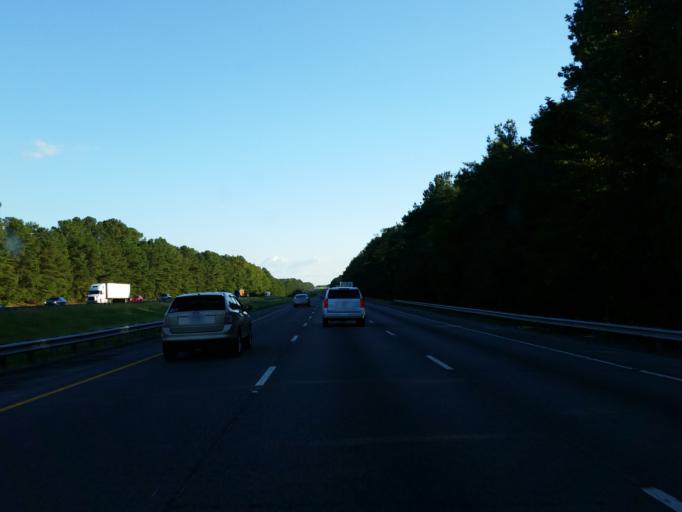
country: US
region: Georgia
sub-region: Houston County
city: Perry
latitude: 32.3735
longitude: -83.7685
